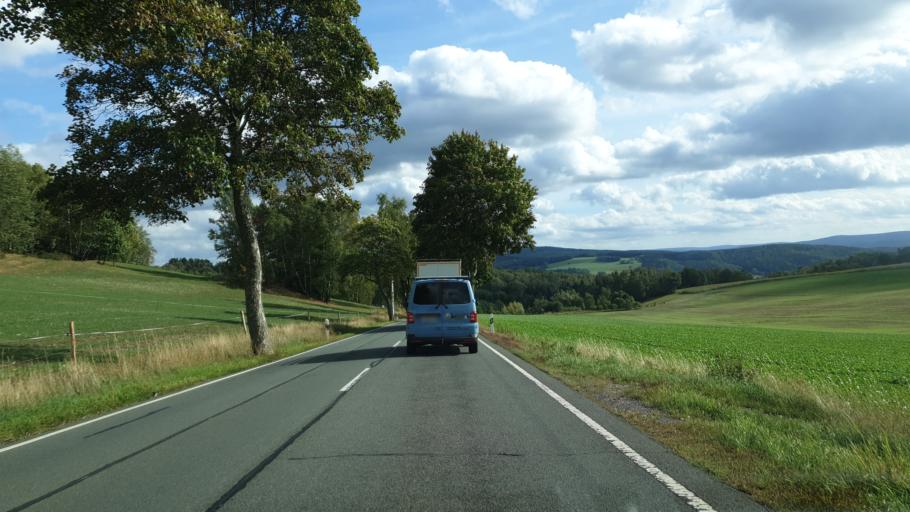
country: DE
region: Saxony
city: Lossnitz
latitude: 50.6436
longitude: 12.7307
